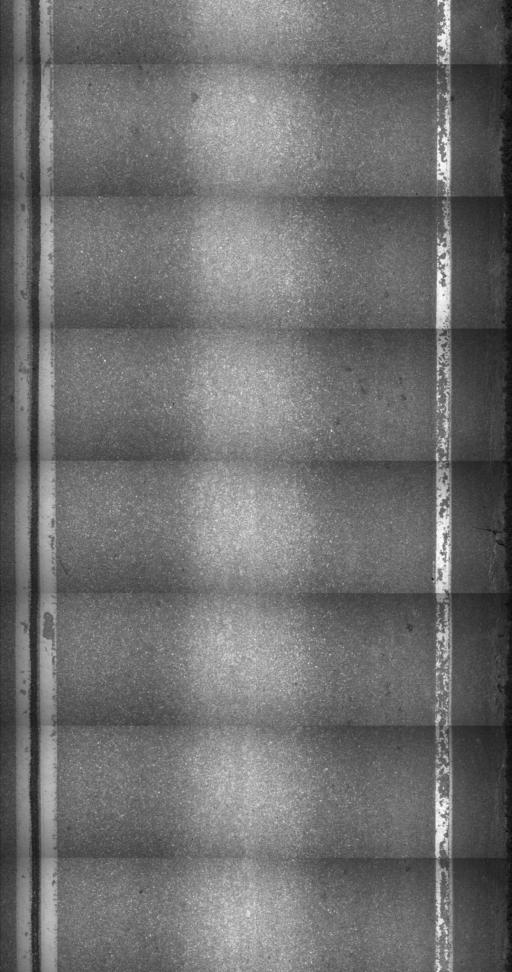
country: US
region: Vermont
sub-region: Chittenden County
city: Milton
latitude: 44.6301
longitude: -73.0190
